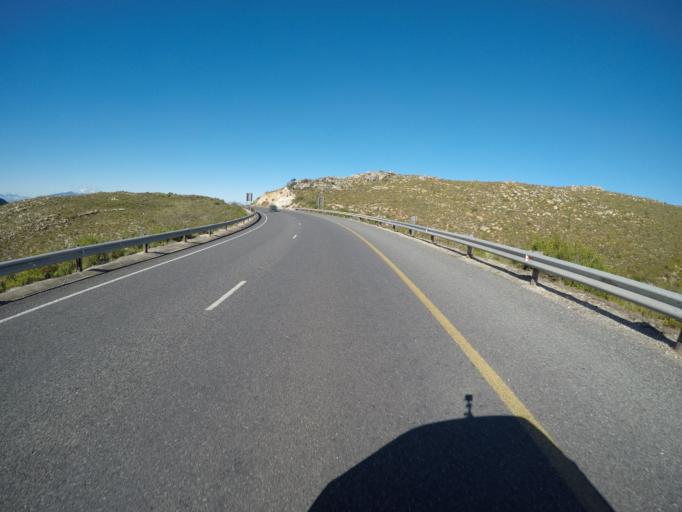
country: ZA
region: Western Cape
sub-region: Overberg District Municipality
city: Grabouw
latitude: -34.2162
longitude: 19.1700
